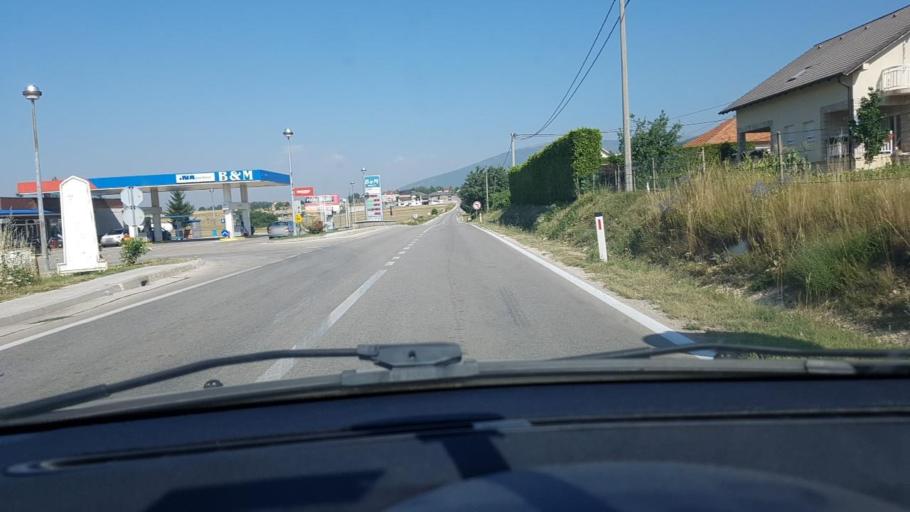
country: BA
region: Federation of Bosnia and Herzegovina
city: Livno
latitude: 43.8397
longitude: 16.9743
